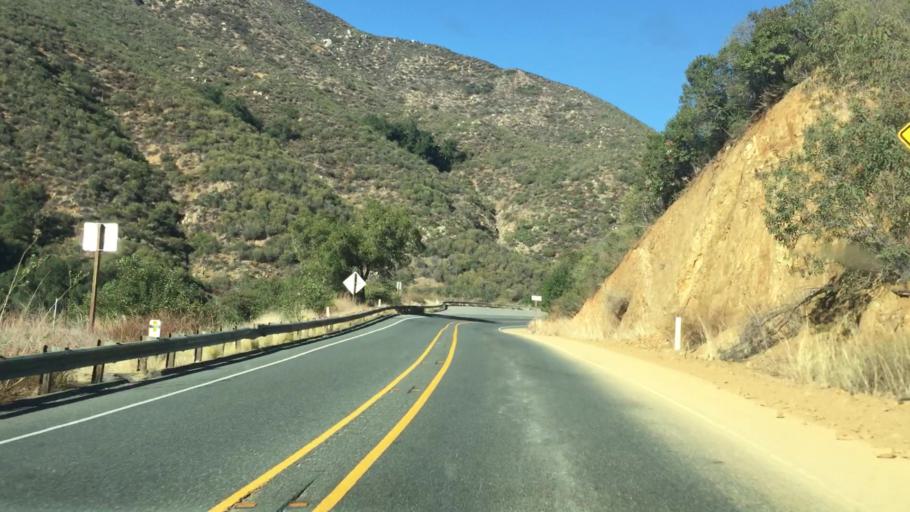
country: US
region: California
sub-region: Orange County
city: Coto De Caza
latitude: 33.5954
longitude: -117.4643
